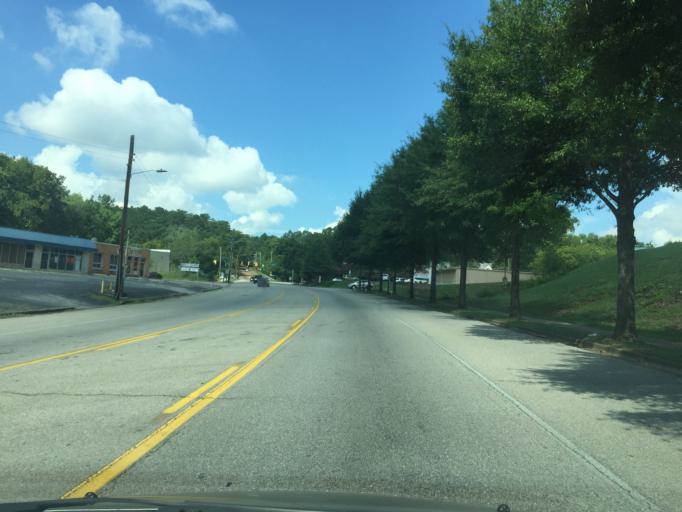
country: US
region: Tennessee
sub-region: Hamilton County
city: East Chattanooga
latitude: 35.0482
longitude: -85.2407
